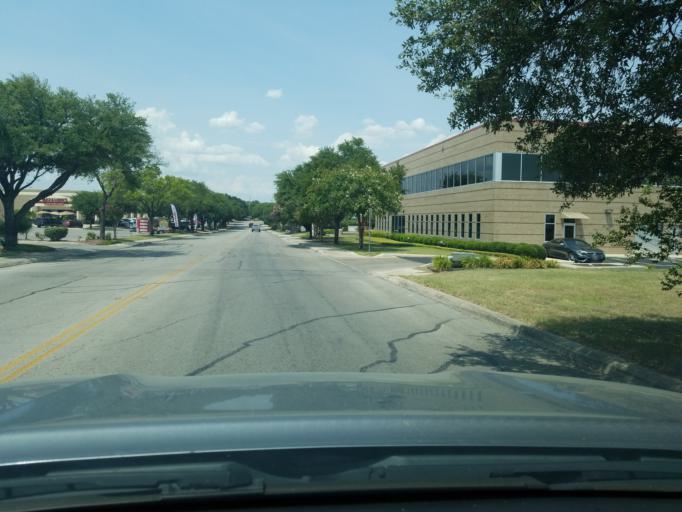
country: US
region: Texas
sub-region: Bexar County
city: Hollywood Park
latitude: 29.5639
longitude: -98.4861
